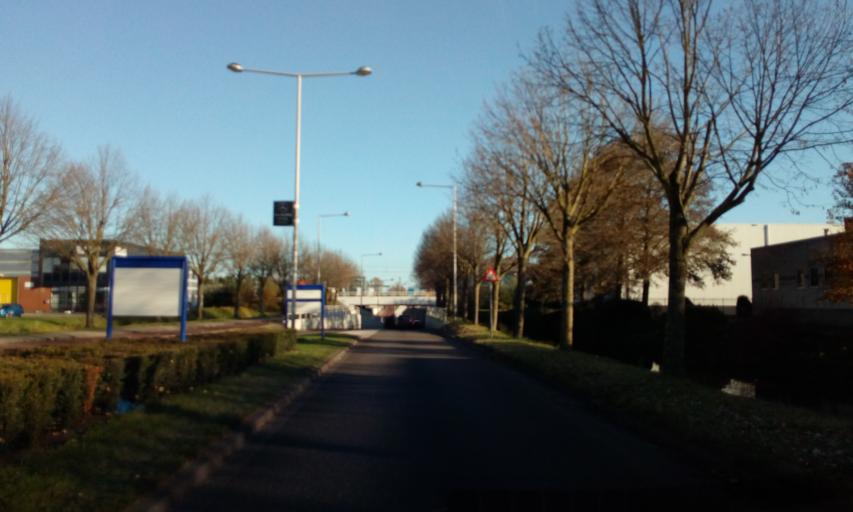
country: NL
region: South Holland
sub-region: Gemeente Leidschendam-Voorburg
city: Voorburg
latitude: 52.0691
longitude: 4.3908
